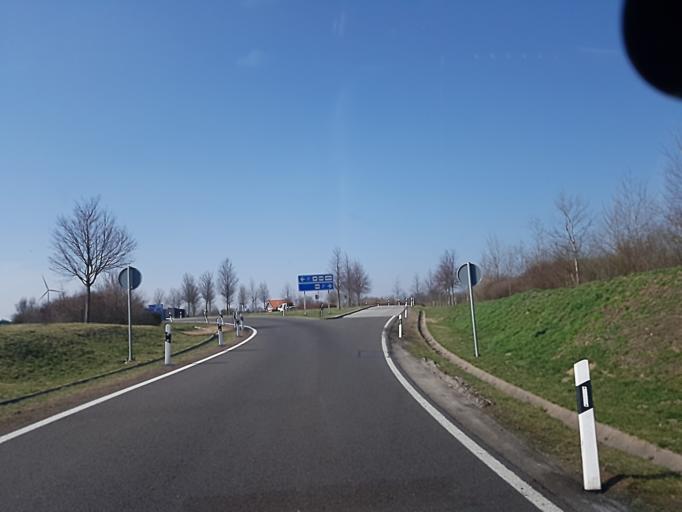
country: DE
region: Brandenburg
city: Vetschau
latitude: 51.7545
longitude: 14.1285
